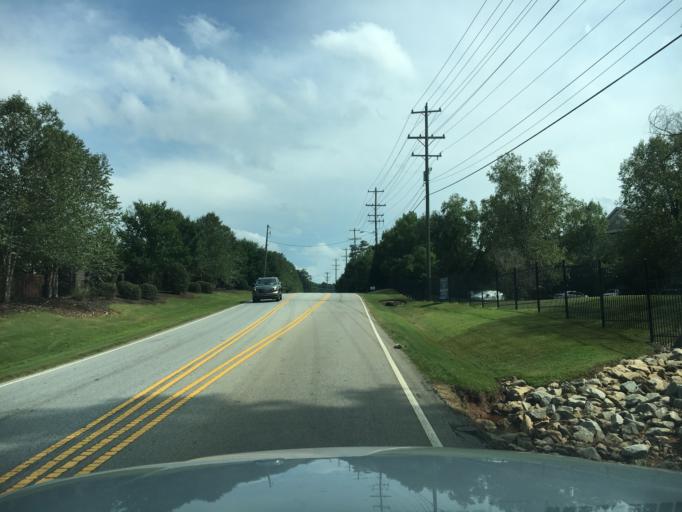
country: US
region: South Carolina
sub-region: Greenville County
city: Wade Hampton
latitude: 34.8482
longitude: -82.3135
